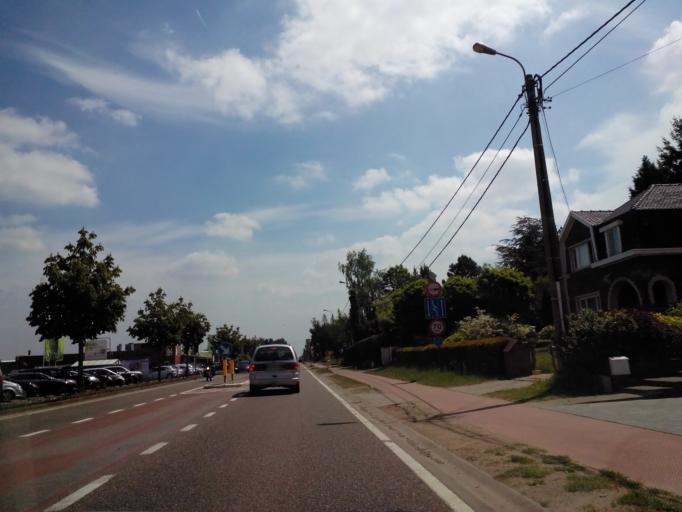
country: BE
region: Flanders
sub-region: Provincie Vlaams-Brabant
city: Aarschot
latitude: 50.9793
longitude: 4.8566
